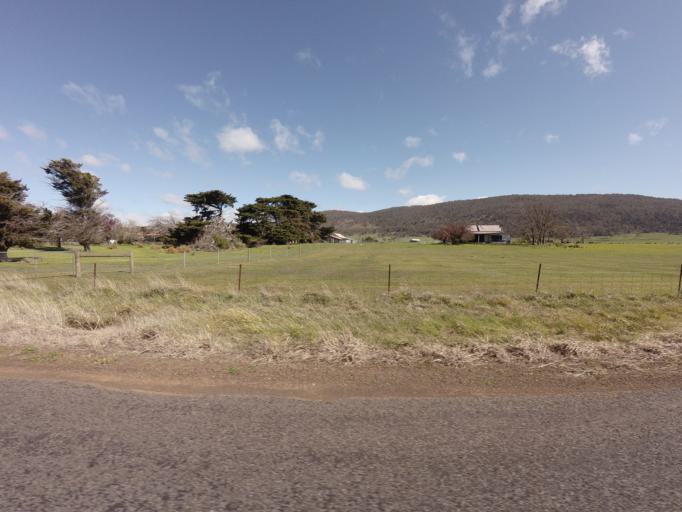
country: AU
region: Tasmania
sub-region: Northern Midlands
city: Evandale
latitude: -41.9815
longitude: 147.4490
